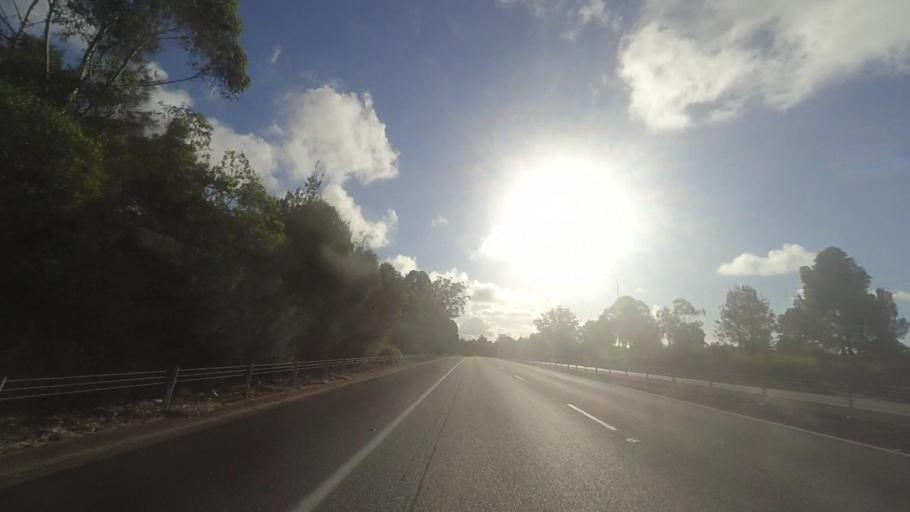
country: AU
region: New South Wales
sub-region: Great Lakes
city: Nabiac
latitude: -32.0948
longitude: 152.3816
